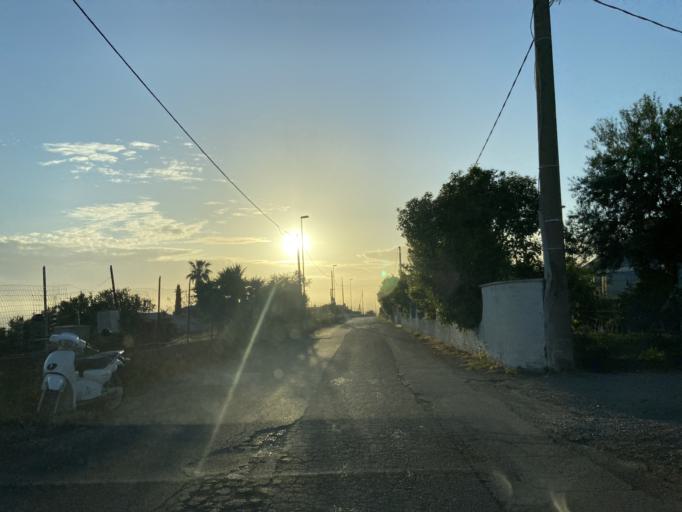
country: IT
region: Latium
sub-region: Citta metropolitana di Roma Capitale
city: Civitavecchia
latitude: 42.0816
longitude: 11.8321
